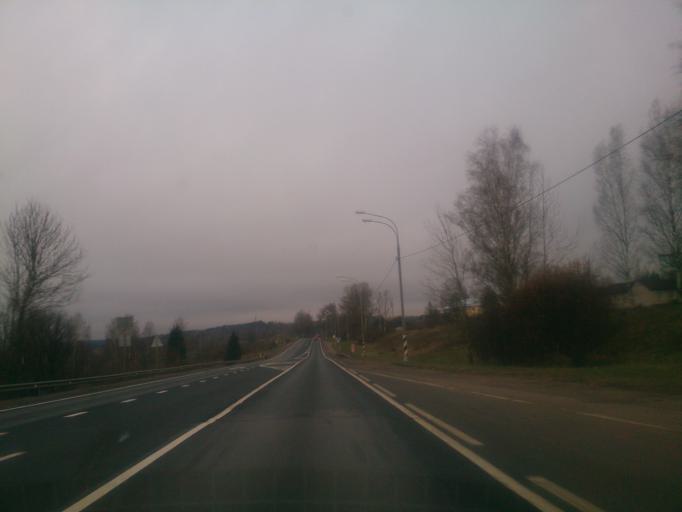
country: RU
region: Novgorod
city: Valday
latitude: 58.0336
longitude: 32.9714
